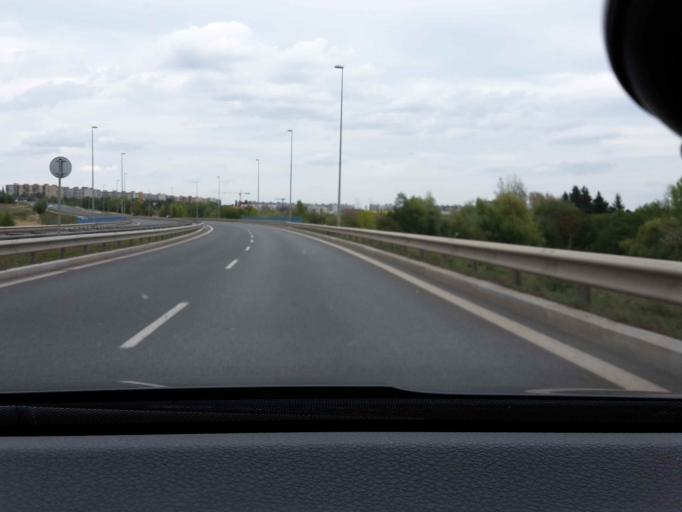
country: CZ
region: Central Bohemia
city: Hostivice
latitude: 50.0386
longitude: 14.3003
